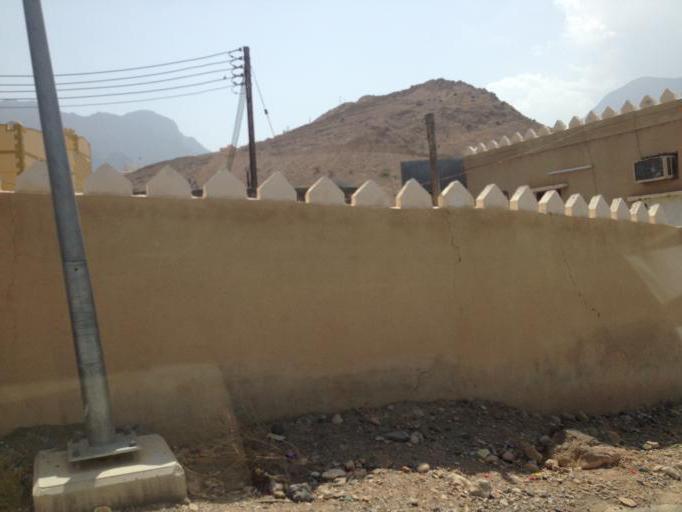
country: OM
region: Ash Sharqiyah
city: Ibra'
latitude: 23.0879
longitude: 58.8532
